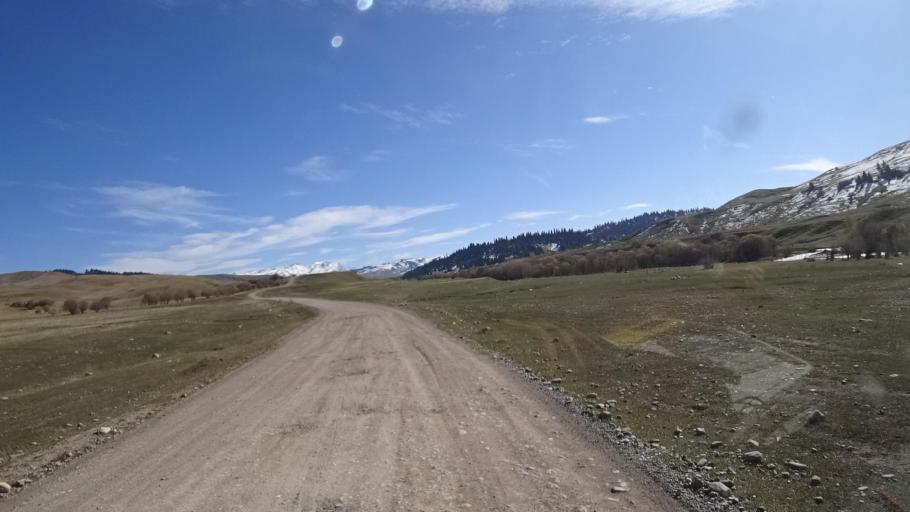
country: KZ
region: Almaty Oblysy
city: Kegen
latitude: 42.7379
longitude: 79.0098
